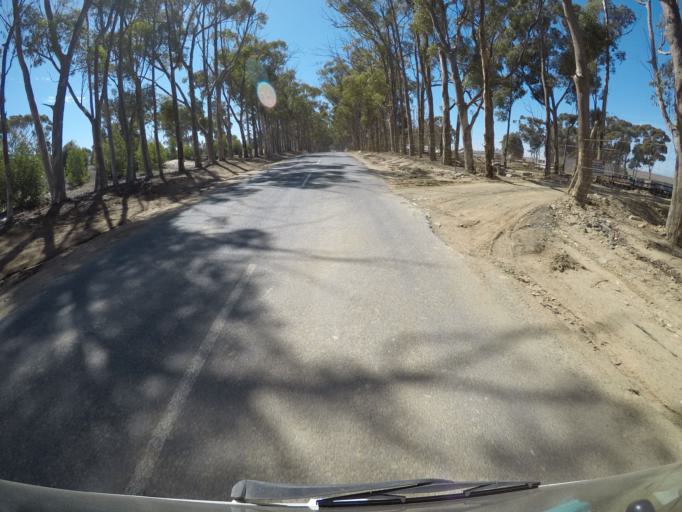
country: ZA
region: Western Cape
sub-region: City of Cape Town
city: Sunset Beach
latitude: -33.7642
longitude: 18.5511
